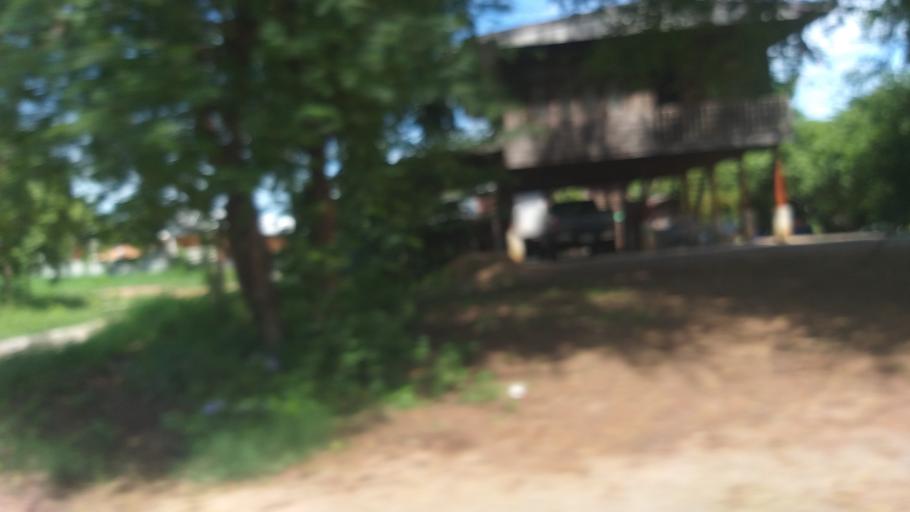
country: TH
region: Khon Kaen
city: Nong Ruea
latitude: 16.4878
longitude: 102.4349
